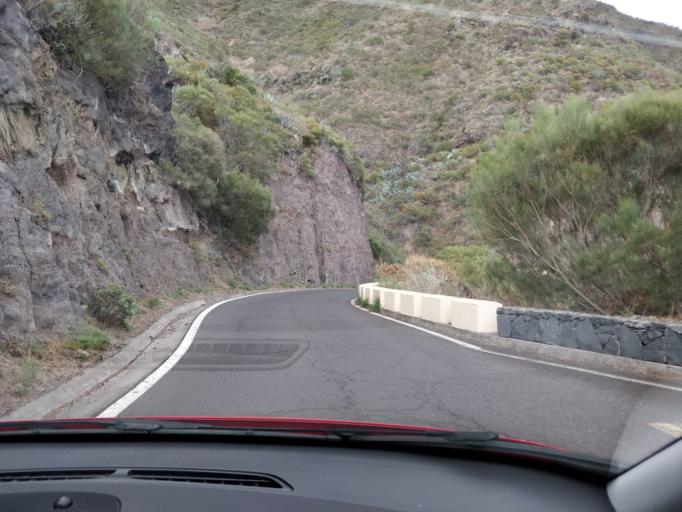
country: ES
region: Canary Islands
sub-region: Provincia de Santa Cruz de Tenerife
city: Santiago del Teide
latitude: 28.3168
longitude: -16.8506
